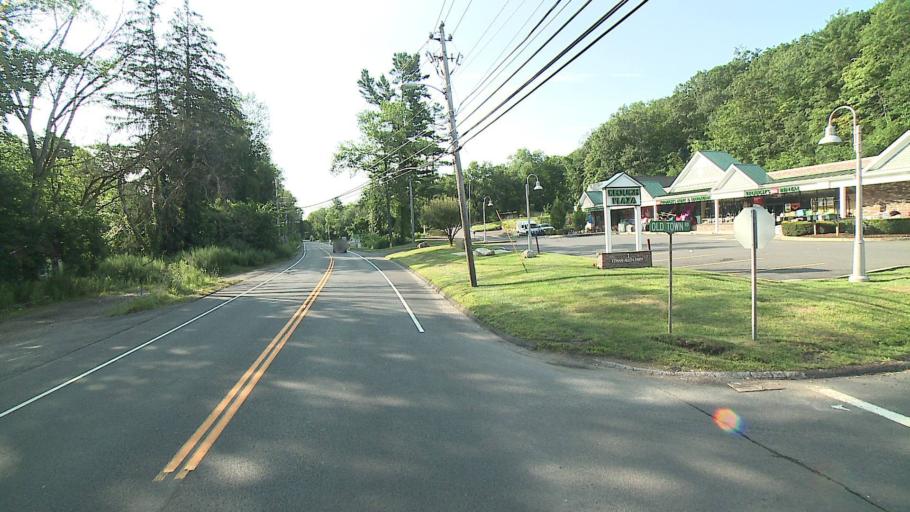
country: US
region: Connecticut
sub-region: Fairfield County
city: Georgetown
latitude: 41.2650
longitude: -73.4406
